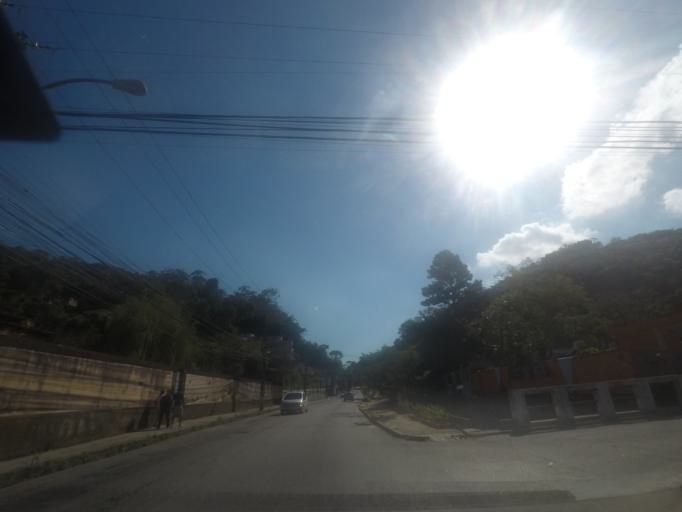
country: BR
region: Rio de Janeiro
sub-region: Petropolis
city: Petropolis
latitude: -22.5296
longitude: -43.1969
